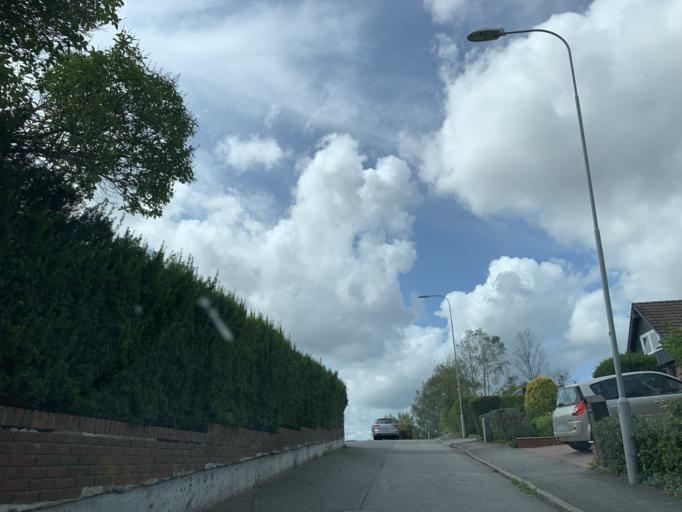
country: SE
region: Vaestra Goetaland
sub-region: Goteborg
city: Eriksbo
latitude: 57.7518
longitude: 12.0547
